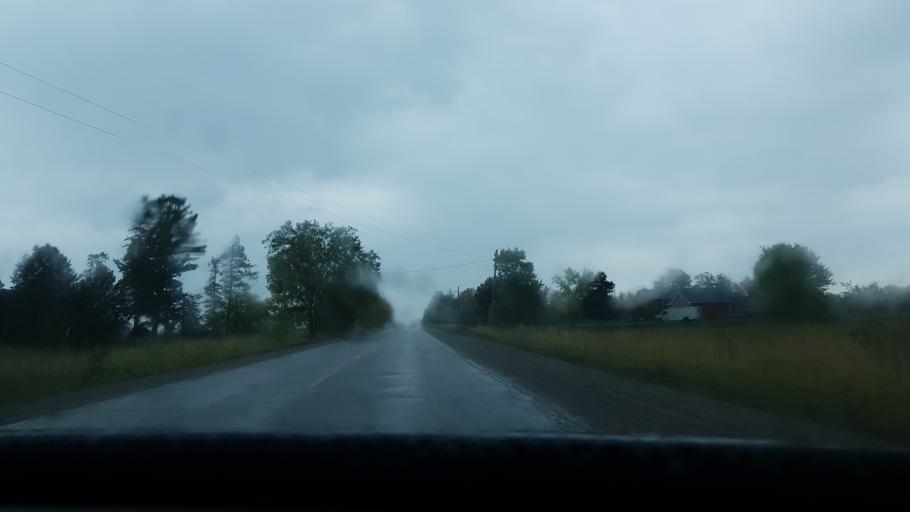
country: CA
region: Ontario
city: Omemee
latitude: 44.3871
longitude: -78.5881
